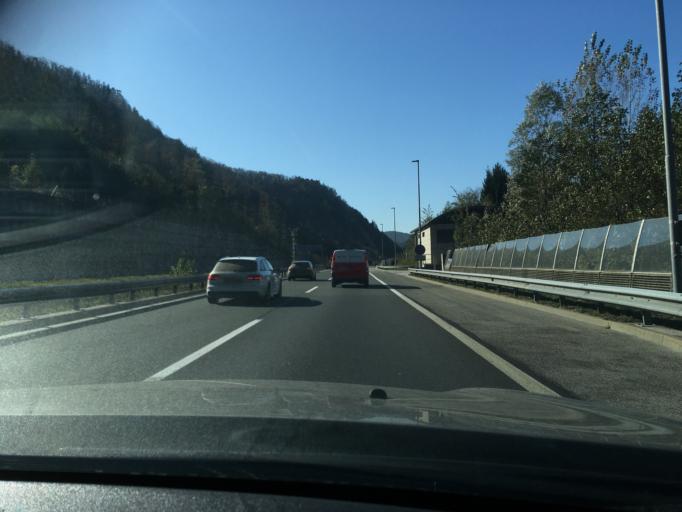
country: SI
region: Zagorje ob Savi
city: Izlake
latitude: 46.1840
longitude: 14.8596
